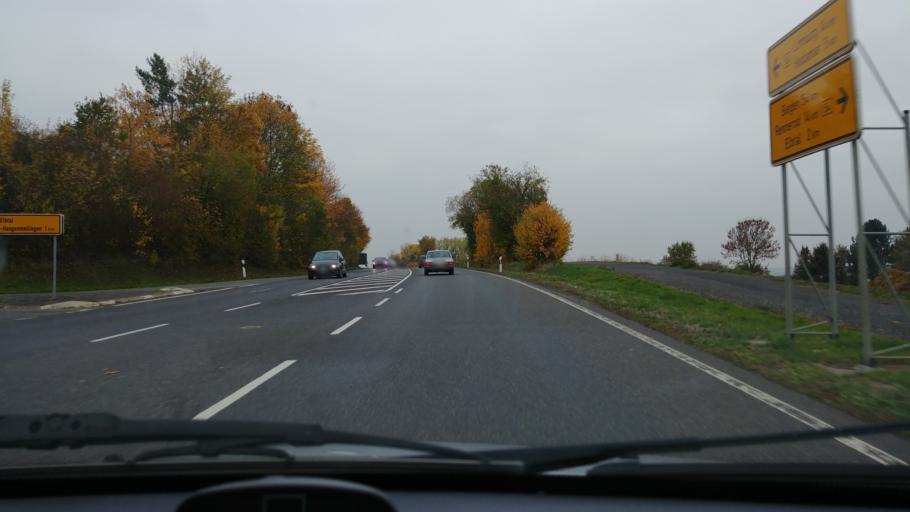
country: DE
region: Hesse
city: Waldbrunn
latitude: 50.4904
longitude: 8.0610
